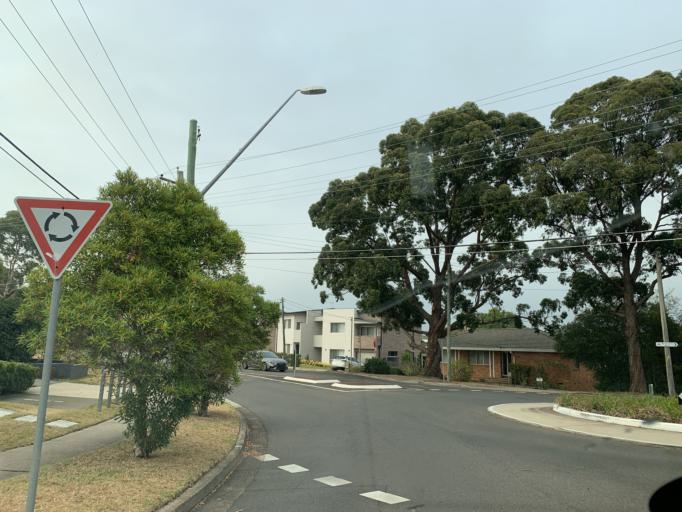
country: AU
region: New South Wales
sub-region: Parramatta
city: Carlingford
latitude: -33.7781
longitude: 151.0609
